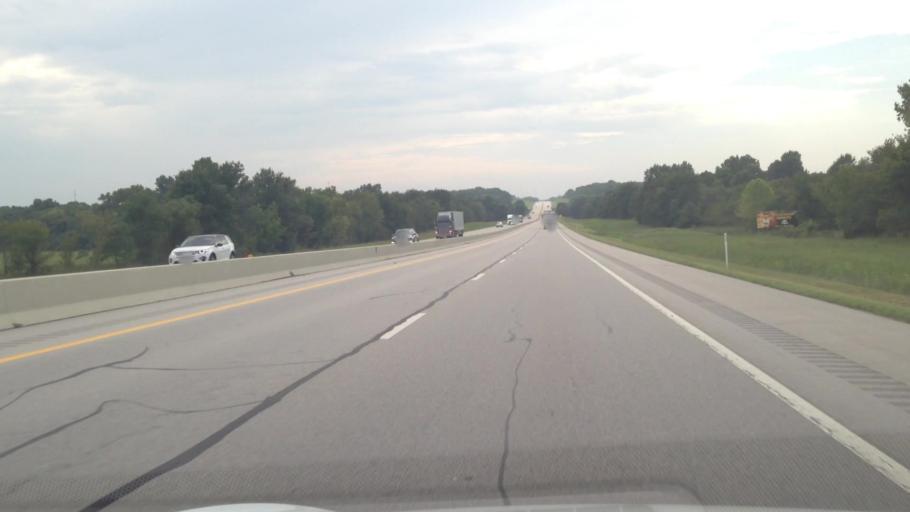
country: US
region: Kansas
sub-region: Cherokee County
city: Baxter Springs
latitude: 36.9291
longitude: -94.7305
